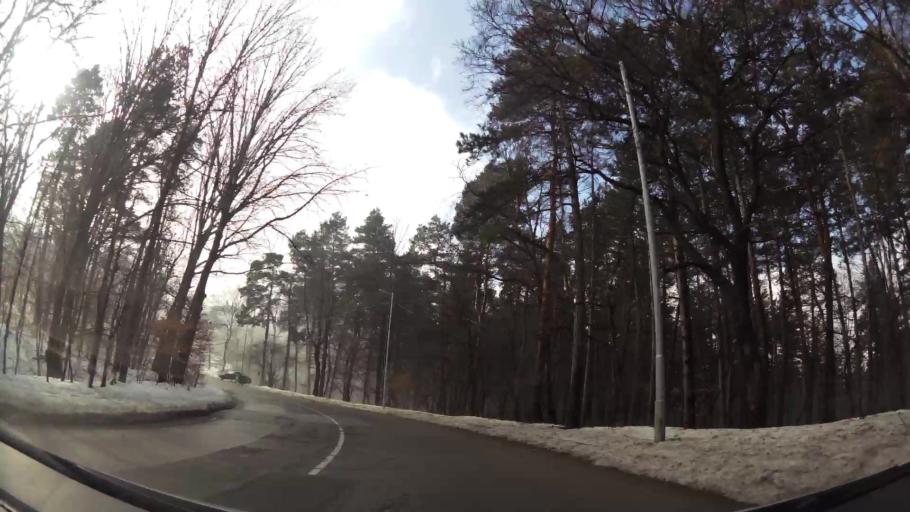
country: BG
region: Sofia-Capital
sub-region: Stolichna Obshtina
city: Sofia
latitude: 42.6497
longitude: 23.2419
